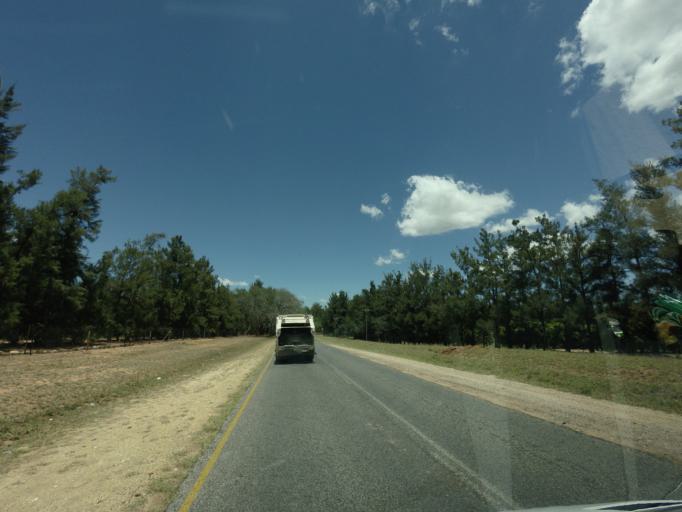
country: ZA
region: Limpopo
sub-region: Mopani District Municipality
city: Hoedspruit
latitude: -24.3923
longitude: 30.8311
